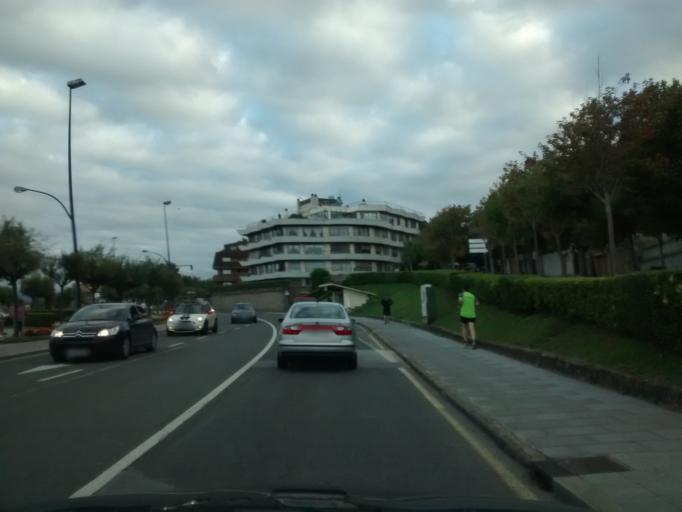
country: ES
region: Cantabria
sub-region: Provincia de Cantabria
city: Santander
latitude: 43.4696
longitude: -3.7773
